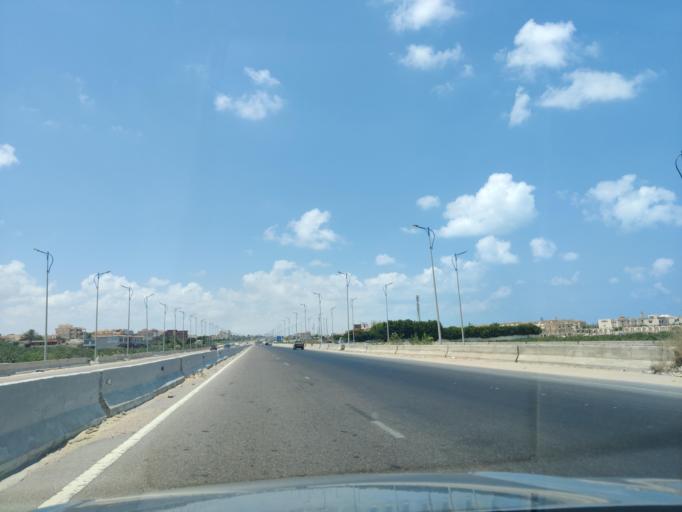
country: EG
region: Alexandria
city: Alexandria
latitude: 30.9797
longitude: 29.5764
